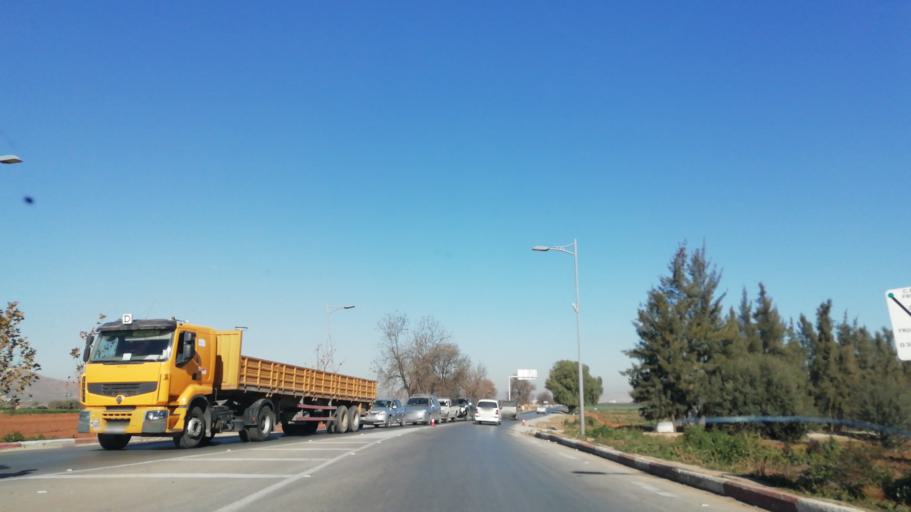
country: DZ
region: Mascara
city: Mascara
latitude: 35.2760
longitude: 0.1285
